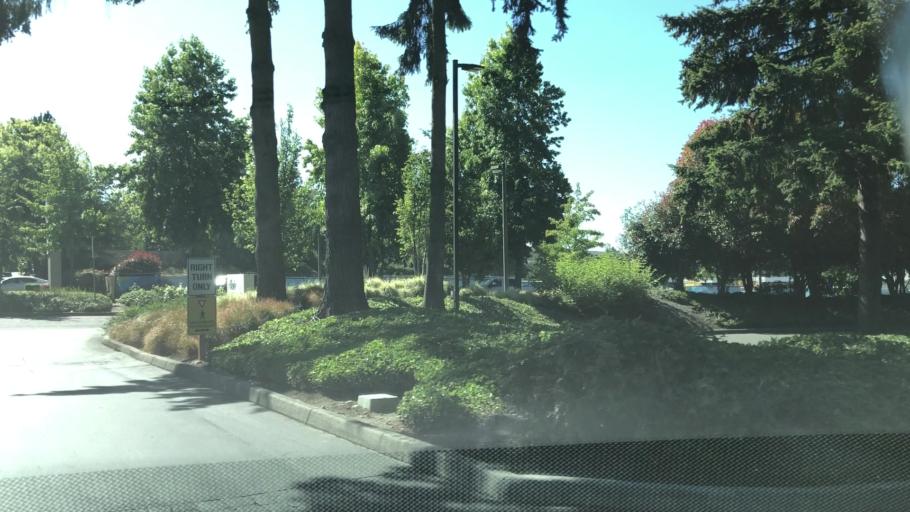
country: US
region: Washington
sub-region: King County
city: SeaTac
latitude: 47.4292
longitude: -122.2948
